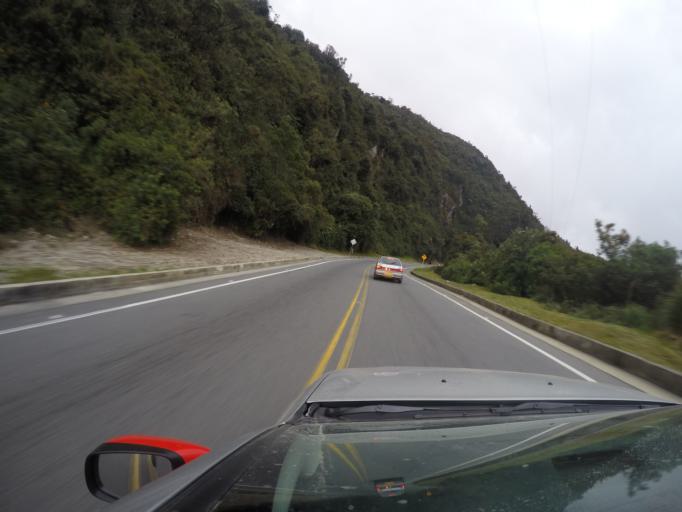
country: CO
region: Tolima
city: Herveo
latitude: 5.0776
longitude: -75.2832
